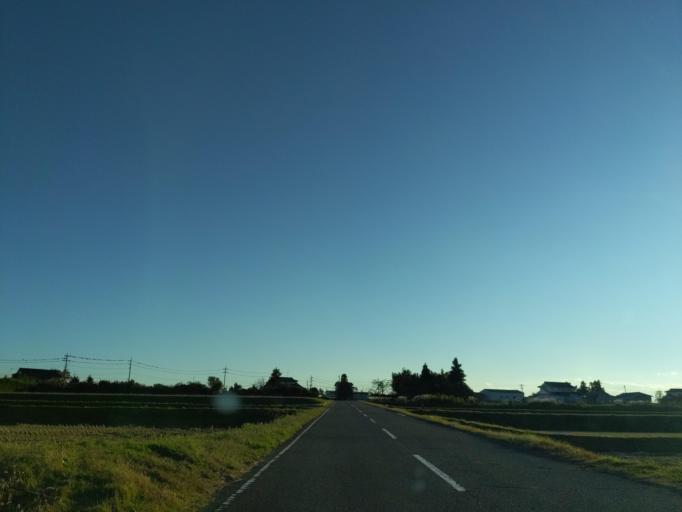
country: JP
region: Fukushima
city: Koriyama
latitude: 37.4418
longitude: 140.3705
